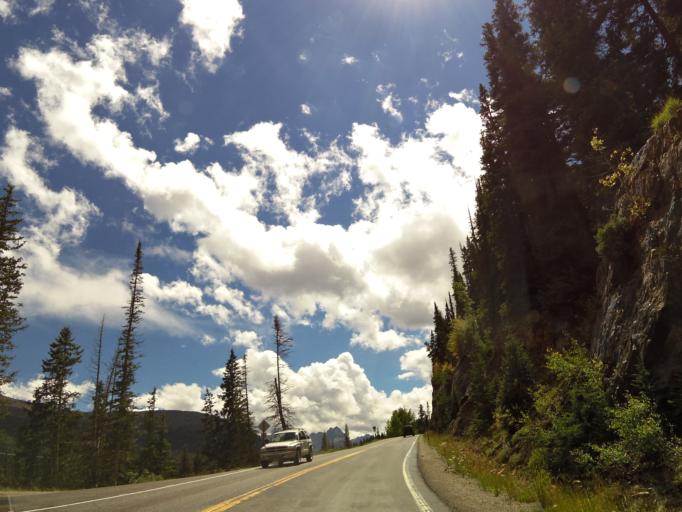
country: US
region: Colorado
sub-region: San Juan County
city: Silverton
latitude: 37.7842
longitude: -107.6718
